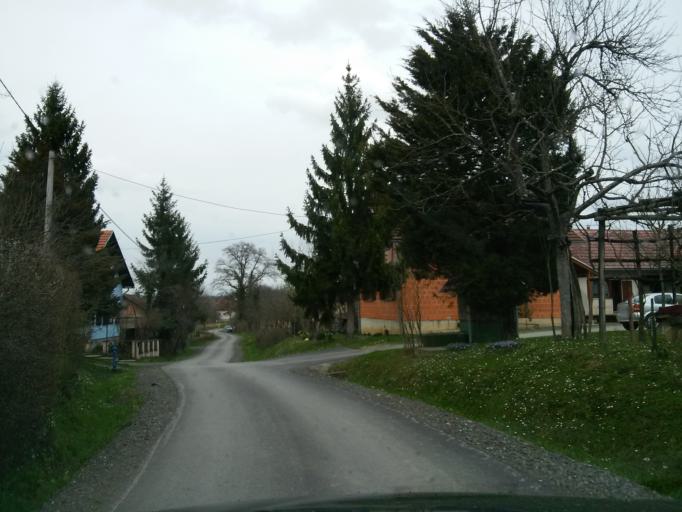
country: HR
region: Sisacko-Moslavacka
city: Glina
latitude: 45.2845
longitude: 15.9904
